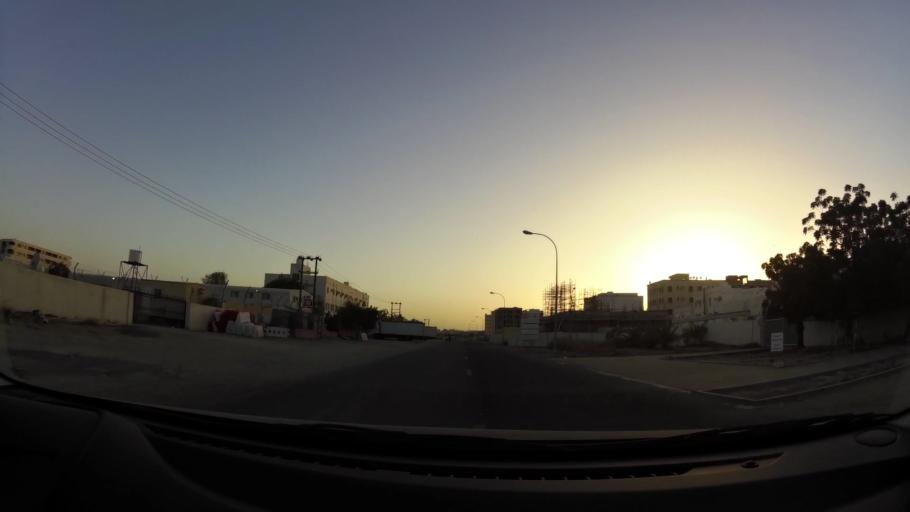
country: OM
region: Muhafazat Masqat
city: As Sib al Jadidah
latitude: 23.5927
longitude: 58.2368
